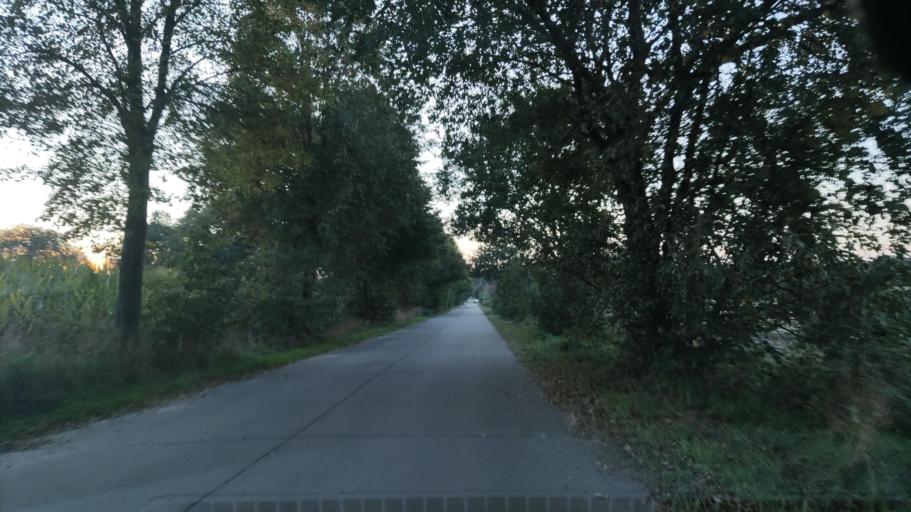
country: DE
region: Lower Saxony
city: Bispingen
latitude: 53.1268
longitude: 10.0092
